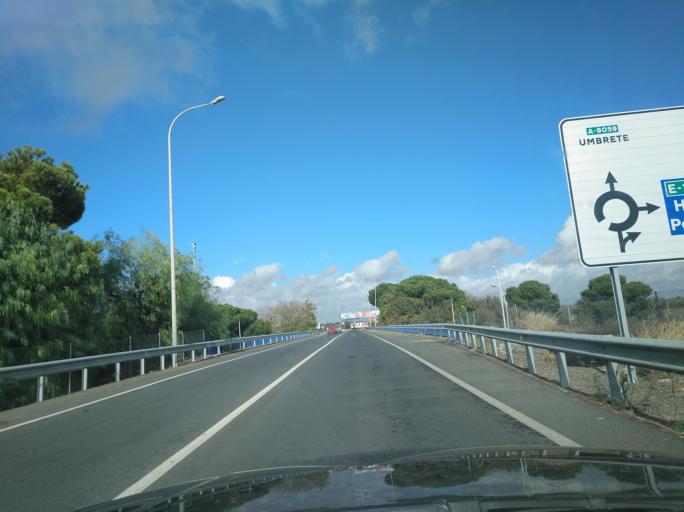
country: ES
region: Andalusia
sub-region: Provincia de Sevilla
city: Umbrete
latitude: 37.3594
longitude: -6.1415
